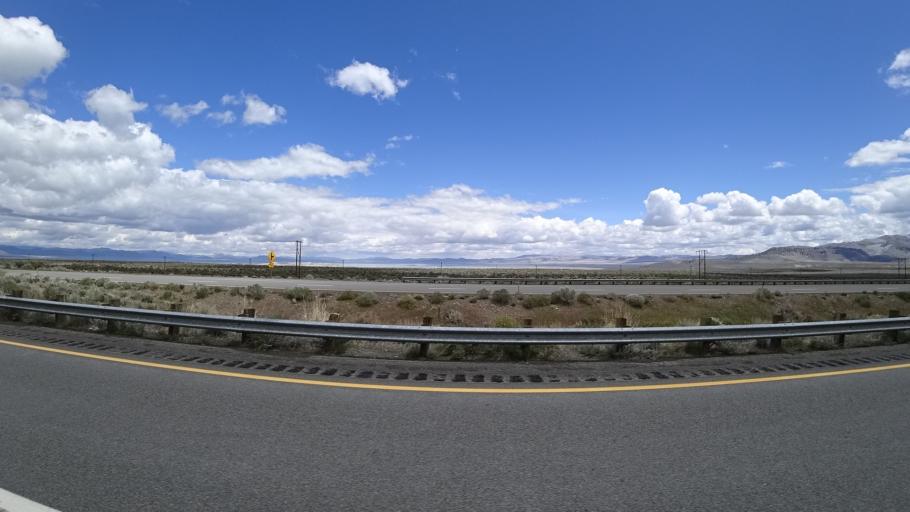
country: US
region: California
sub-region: Mono County
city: Mammoth Lakes
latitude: 37.9418
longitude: -119.1029
